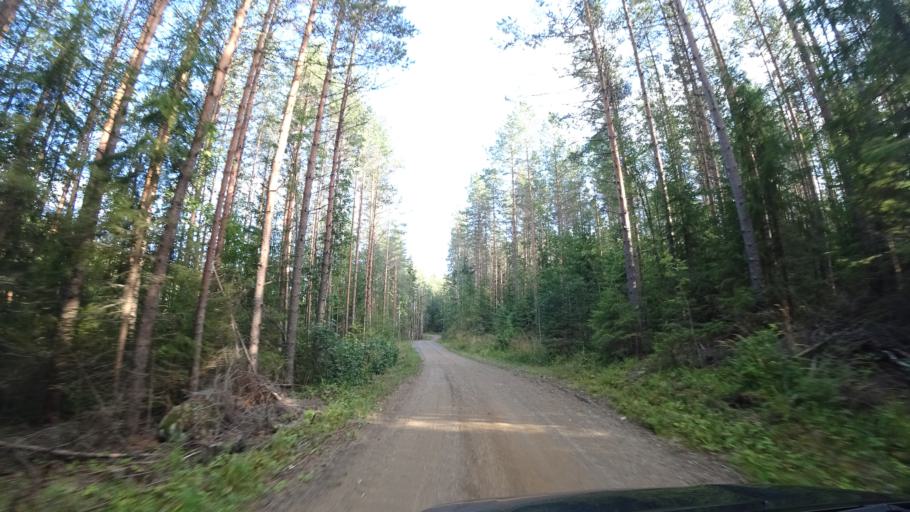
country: FI
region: Paijanne Tavastia
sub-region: Lahti
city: Auttoinen
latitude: 61.2228
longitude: 25.1982
